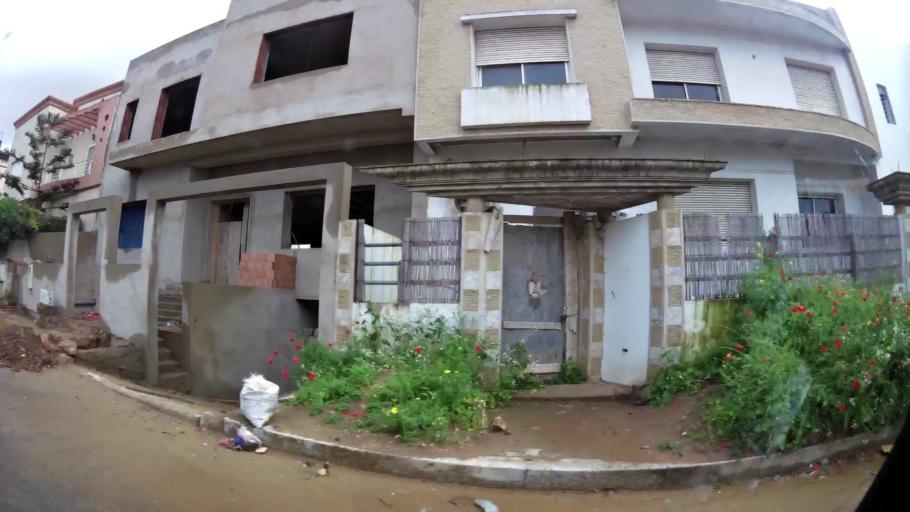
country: MA
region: Grand Casablanca
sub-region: Casablanca
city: Casablanca
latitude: 33.5282
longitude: -7.6432
